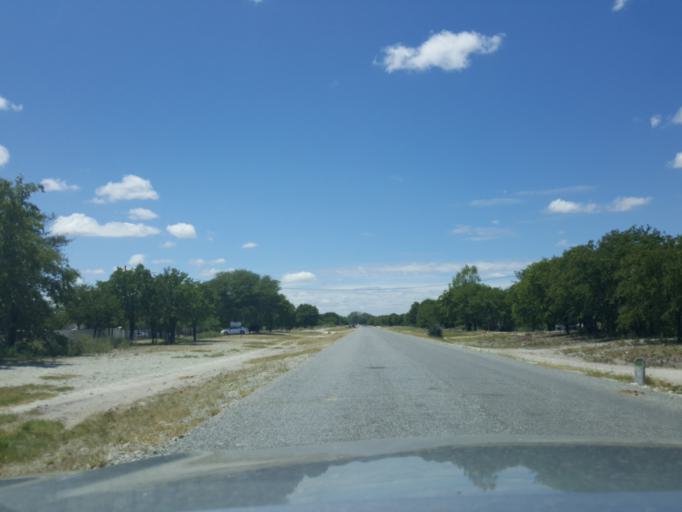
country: BW
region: Central
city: Nata
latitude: -20.2131
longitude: 26.1716
